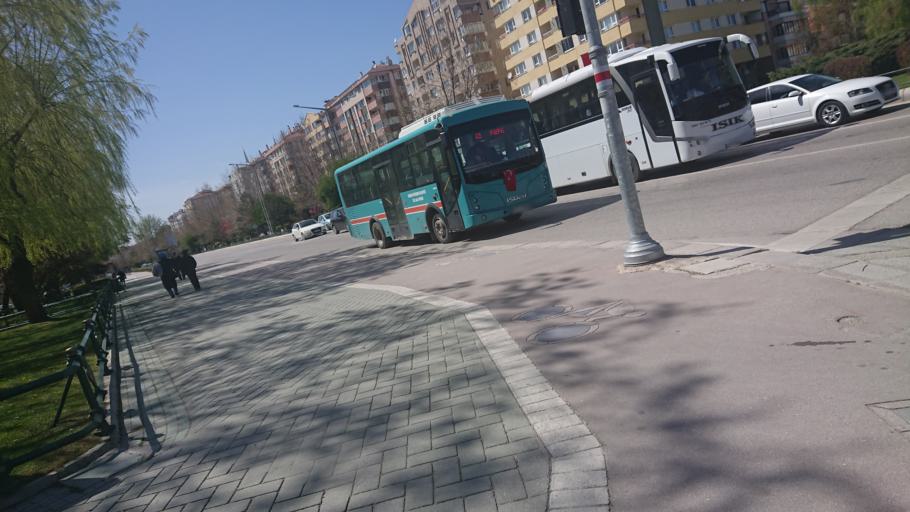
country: TR
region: Eskisehir
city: Eskisehir
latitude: 39.7648
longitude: 30.5092
